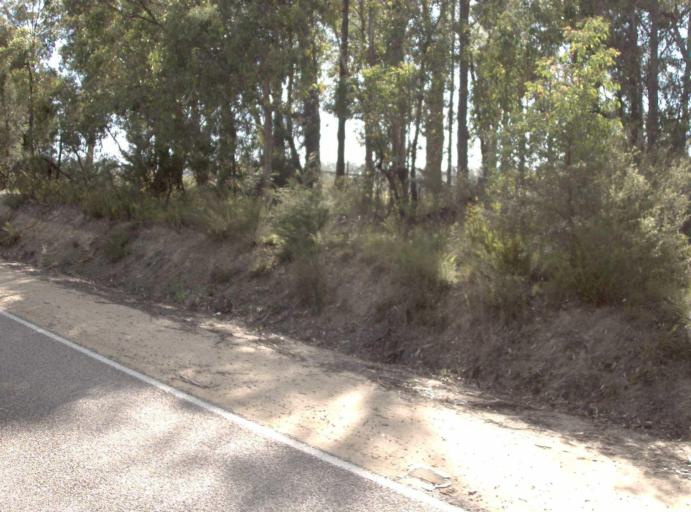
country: AU
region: Victoria
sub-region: East Gippsland
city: Lakes Entrance
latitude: -37.5329
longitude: 148.1522
